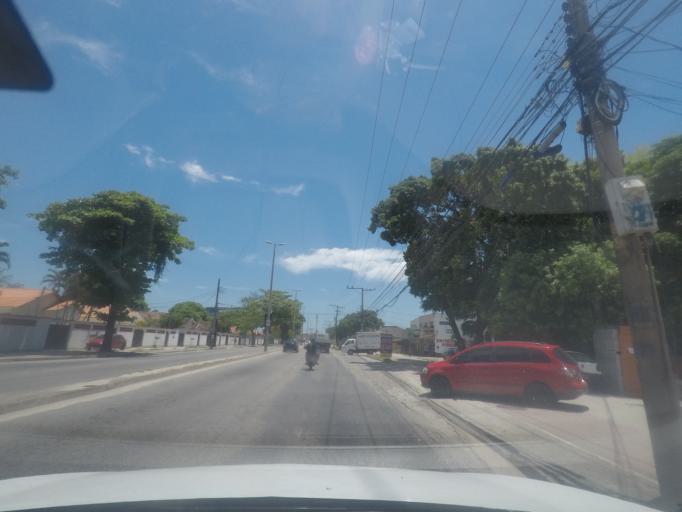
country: BR
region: Rio de Janeiro
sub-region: Itaguai
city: Itaguai
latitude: -22.9085
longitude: -43.6862
